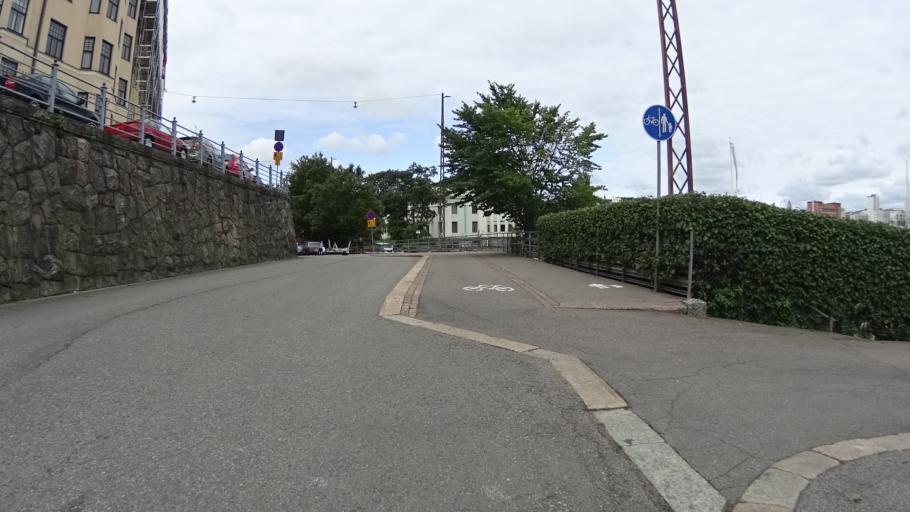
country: FI
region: Uusimaa
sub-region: Helsinki
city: Helsinki
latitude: 60.1688
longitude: 24.9673
